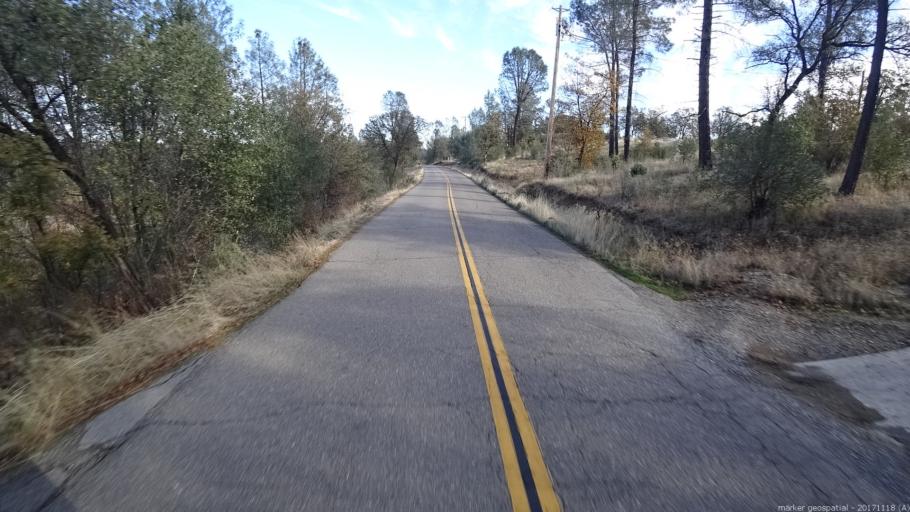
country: US
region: California
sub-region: Shasta County
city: Anderson
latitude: 40.4726
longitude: -122.4019
